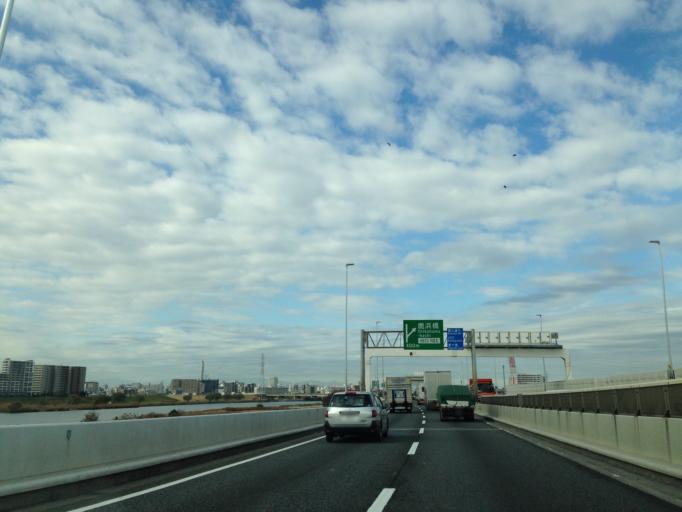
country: JP
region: Saitama
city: Kawaguchi
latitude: 35.7726
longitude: 139.7570
